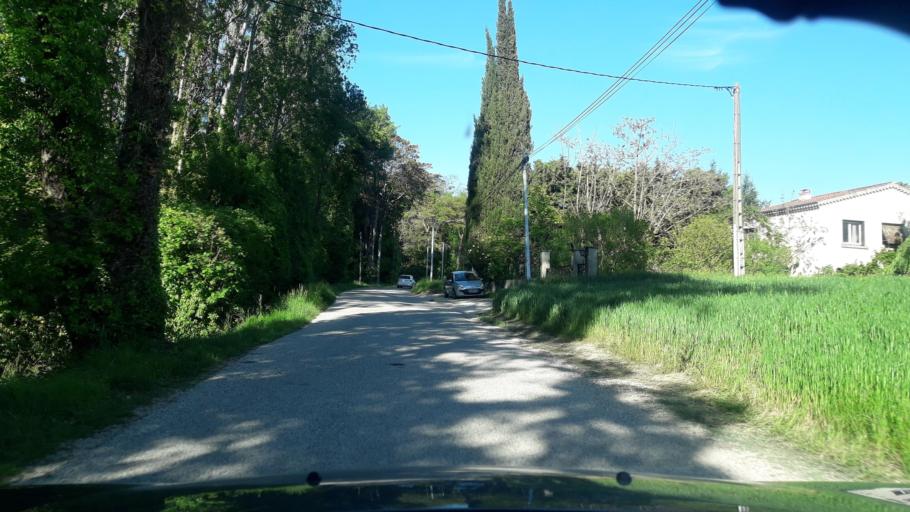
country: FR
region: Rhone-Alpes
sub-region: Departement de la Drome
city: Saulce-sur-Rhone
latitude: 44.7040
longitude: 4.8561
